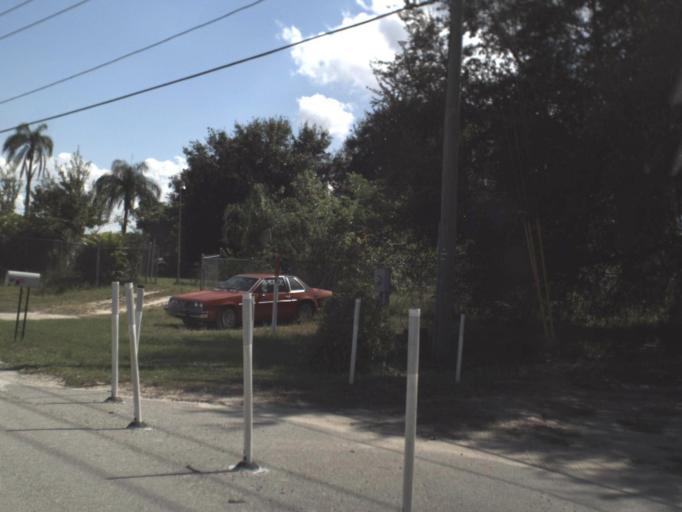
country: US
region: Florida
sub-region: Highlands County
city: Sebring
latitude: 27.4267
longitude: -81.4081
